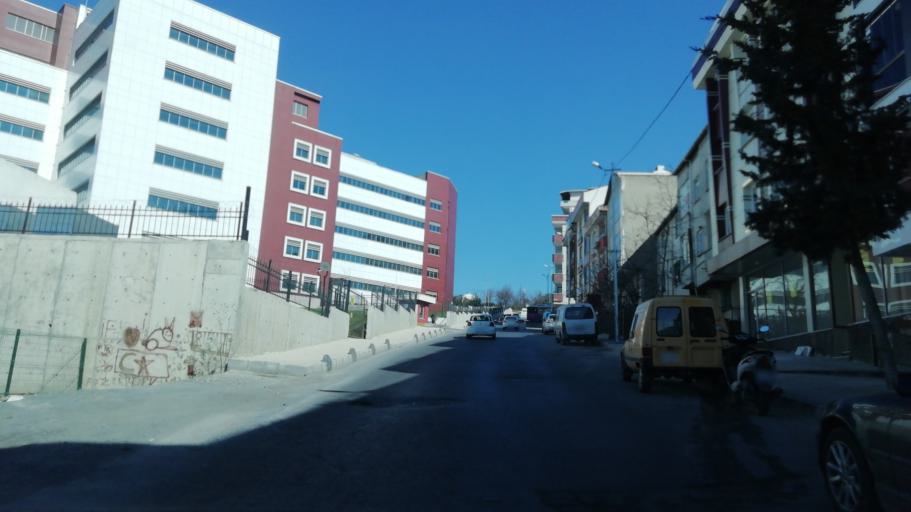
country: TR
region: Istanbul
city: Mahmutbey
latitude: 41.0323
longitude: 28.7755
